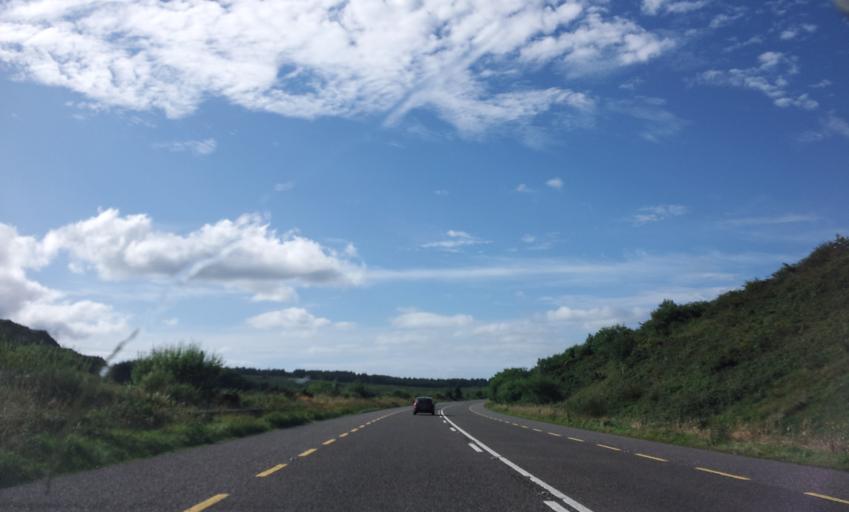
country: IE
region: Munster
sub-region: County Cork
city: Millstreet
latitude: 51.9616
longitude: -9.2415
